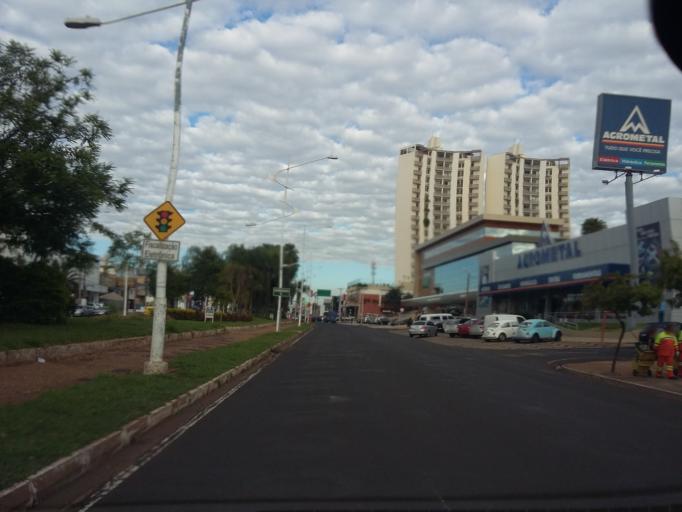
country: BR
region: Sao Paulo
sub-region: Sao Jose Do Rio Preto
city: Sao Jose do Rio Preto
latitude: -20.8187
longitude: -49.3964
